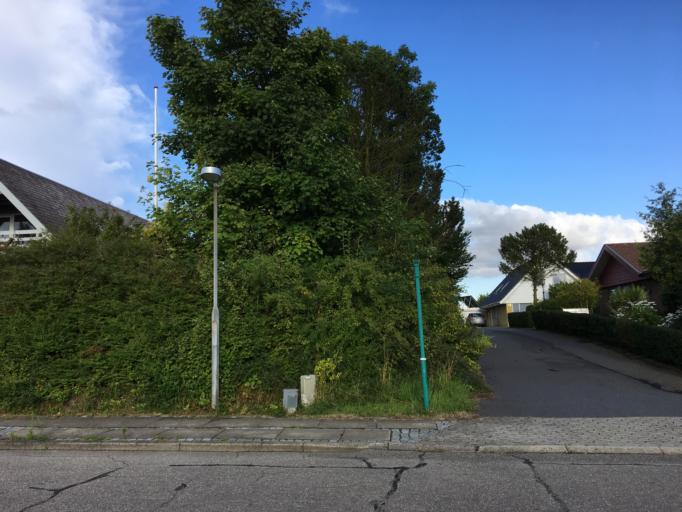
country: DK
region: South Denmark
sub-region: Middelfart Kommune
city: Middelfart
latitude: 55.5048
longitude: 9.7106
